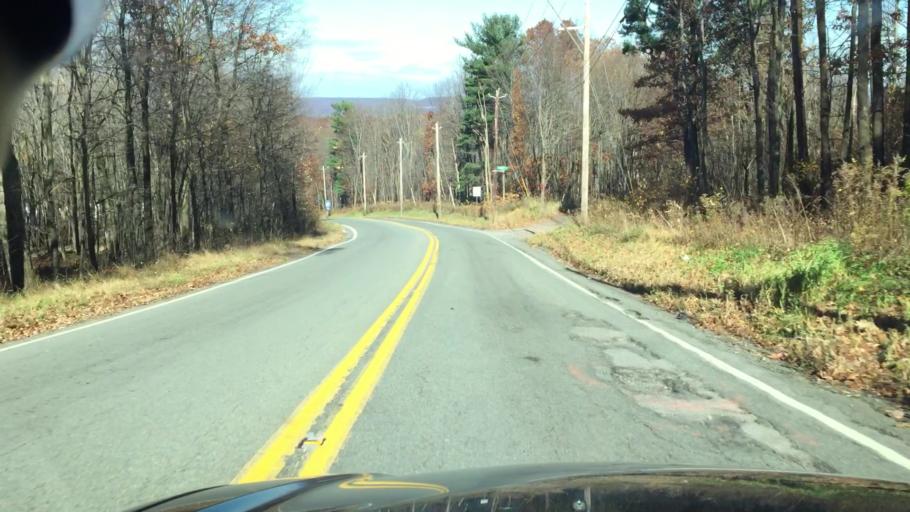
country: US
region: Pennsylvania
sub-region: Luzerne County
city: Freeland
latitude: 41.0804
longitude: -75.9578
